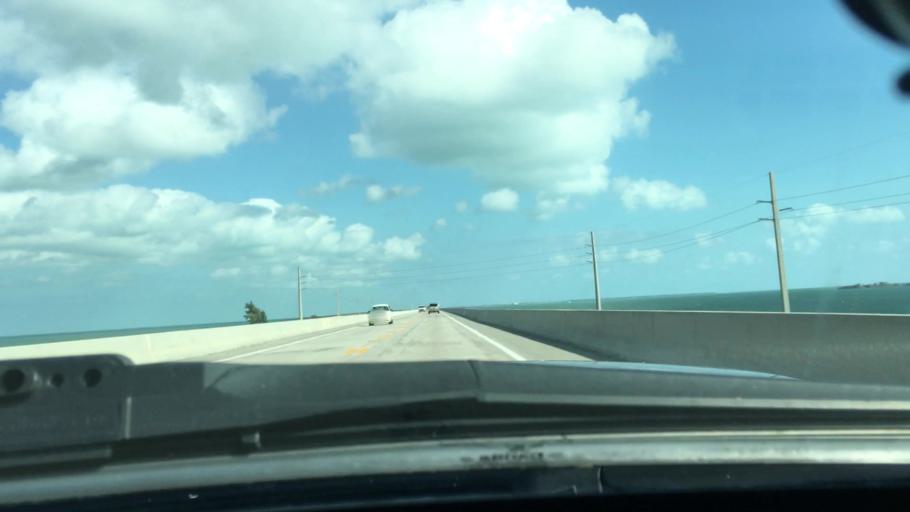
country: US
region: Florida
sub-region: Monroe County
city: Marathon
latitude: 24.6881
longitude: -81.2079
